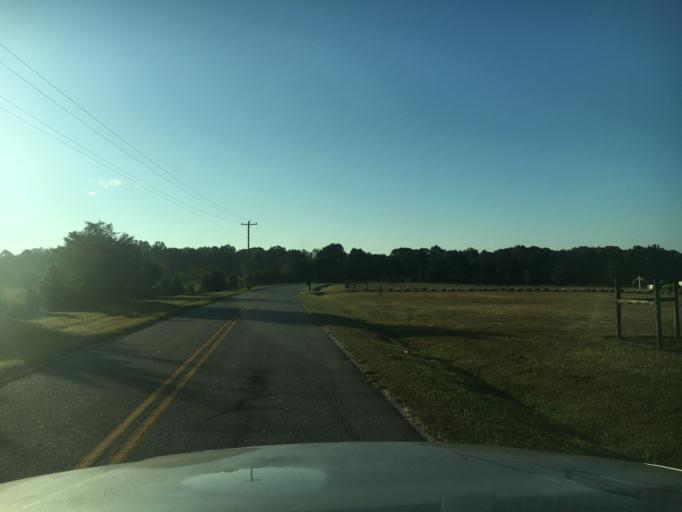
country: US
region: South Carolina
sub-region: Spartanburg County
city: Woodruff
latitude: 34.7915
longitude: -82.0085
